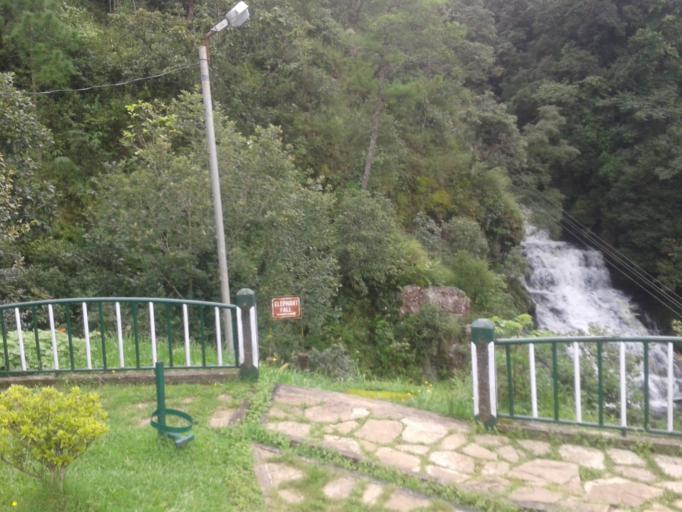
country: IN
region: Meghalaya
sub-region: East Khasi Hills
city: Shillong
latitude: 25.5384
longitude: 91.8220
